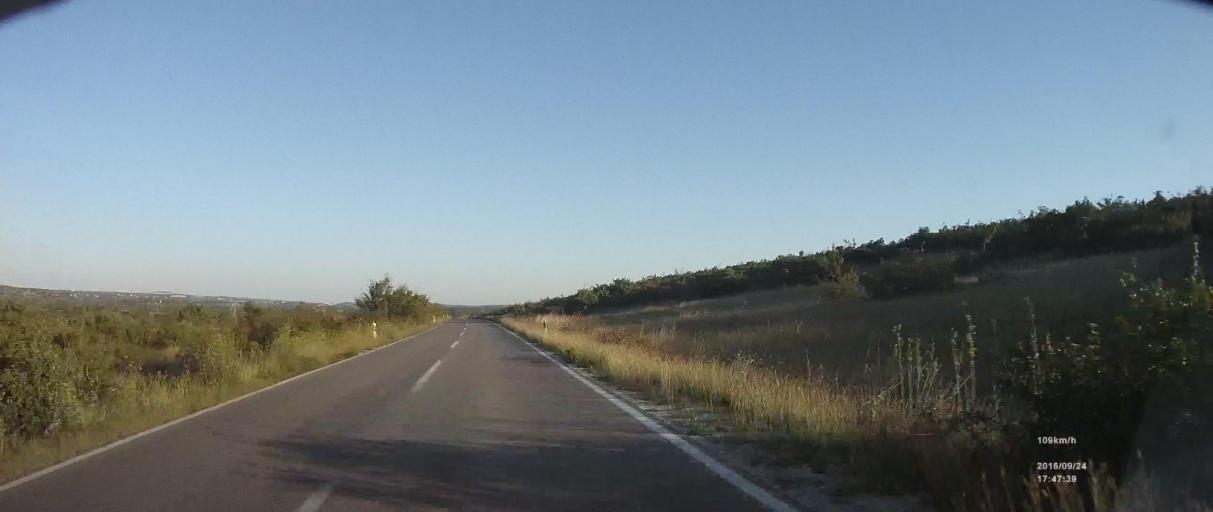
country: HR
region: Zadarska
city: Polaca
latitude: 44.0726
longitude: 15.5262
